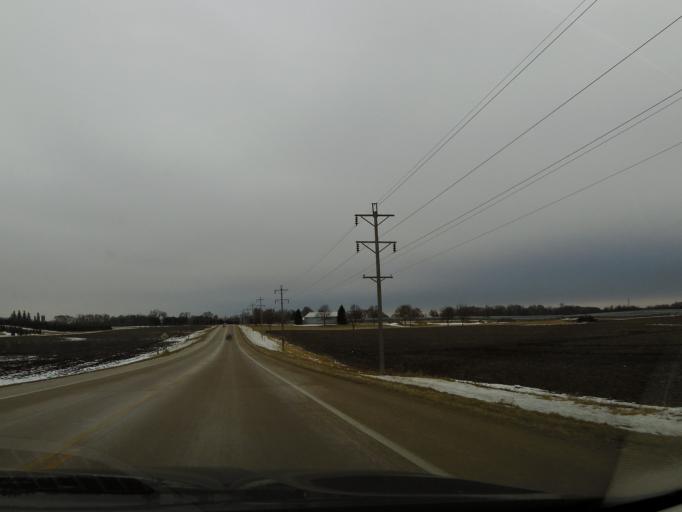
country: US
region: Minnesota
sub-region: Carver County
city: Watertown
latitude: 44.9412
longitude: -93.8313
